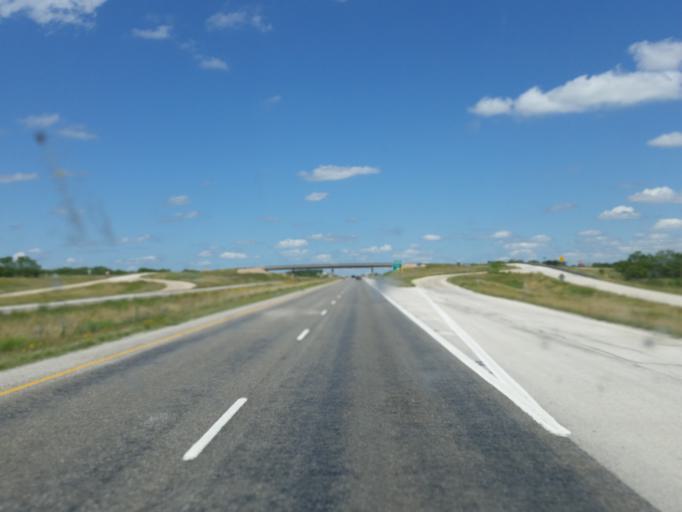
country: US
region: Texas
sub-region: Eastland County
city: Cisco
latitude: 32.3768
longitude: -99.1082
